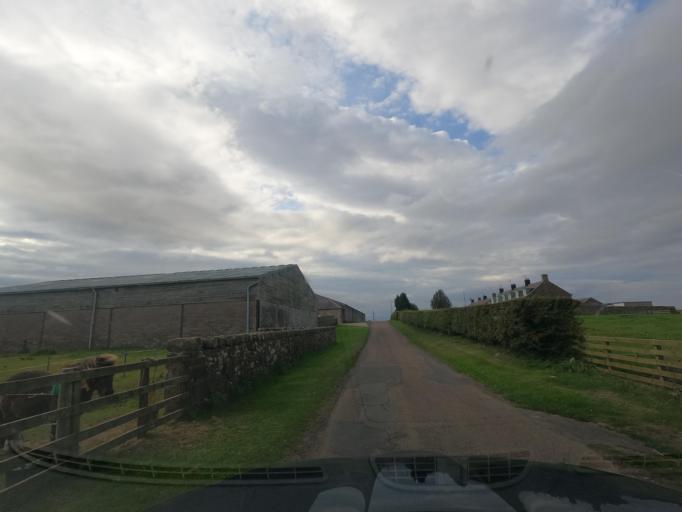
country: GB
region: England
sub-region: Northumberland
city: Ancroft
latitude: 55.7201
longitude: -2.0598
